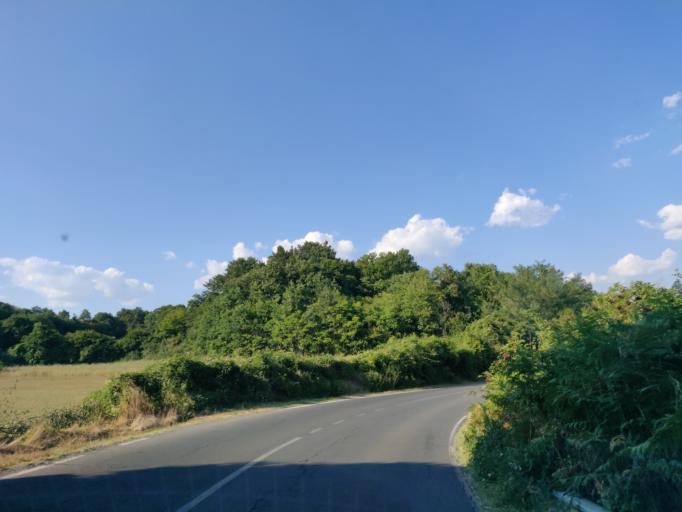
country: IT
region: Latium
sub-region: Provincia di Viterbo
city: Gradoli
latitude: 42.6521
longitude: 11.8434
